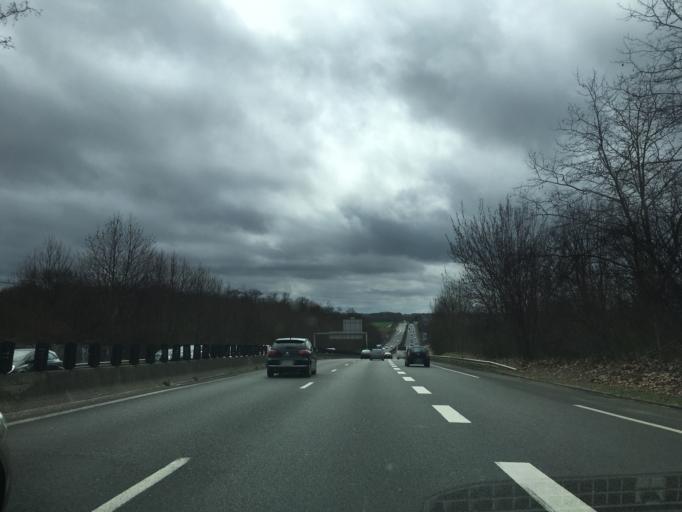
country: FR
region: Ile-de-France
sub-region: Departement de Seine-et-Marne
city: Brie-Comte-Robert
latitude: 48.6750
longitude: 2.6106
